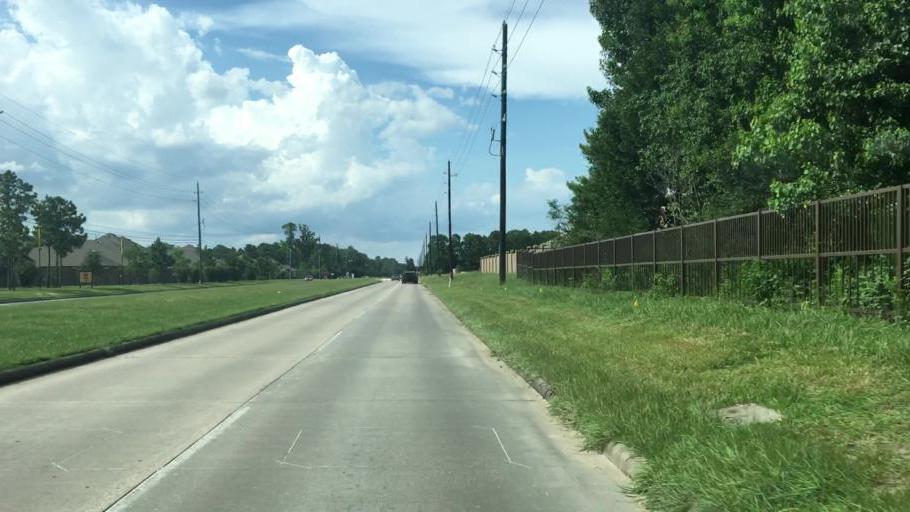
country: US
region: Texas
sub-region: Harris County
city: Atascocita
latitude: 29.9449
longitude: -95.1752
